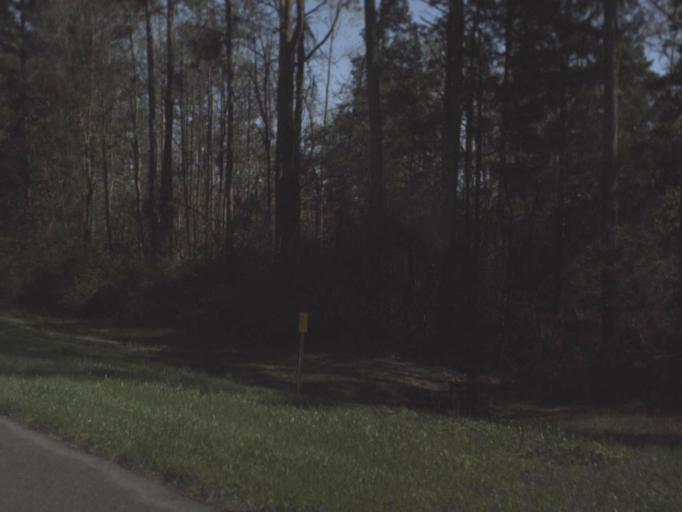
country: US
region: Florida
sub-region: Walton County
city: DeFuniak Springs
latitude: 30.7248
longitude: -85.9596
